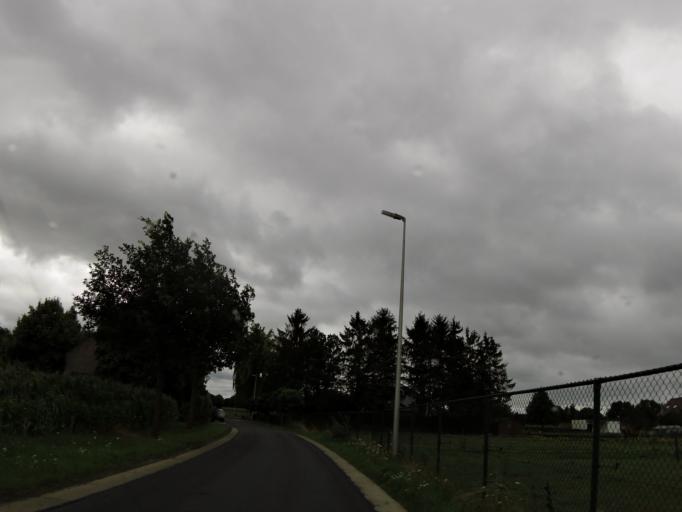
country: BE
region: Flanders
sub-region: Provincie Limburg
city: Maaseik
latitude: 51.0937
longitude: 5.7587
